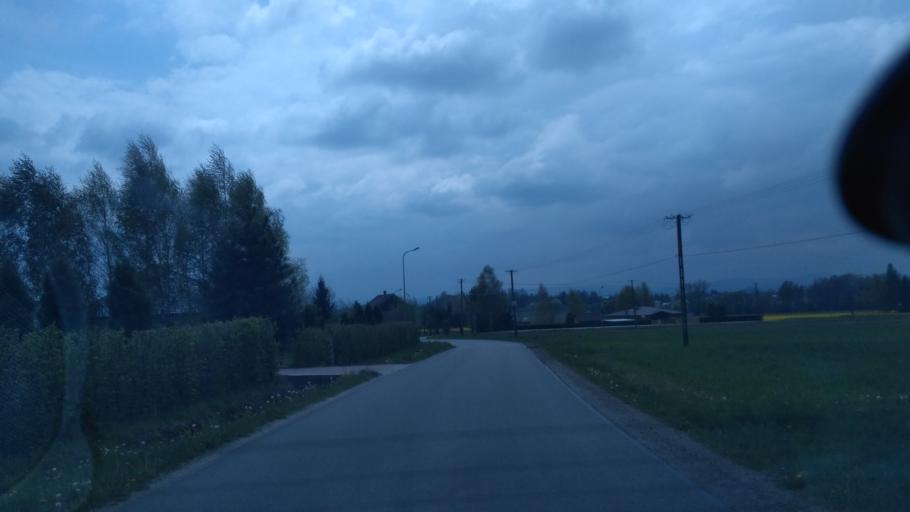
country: PL
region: Subcarpathian Voivodeship
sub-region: Powiat brzozowski
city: Haczow
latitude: 49.6778
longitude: 21.9012
